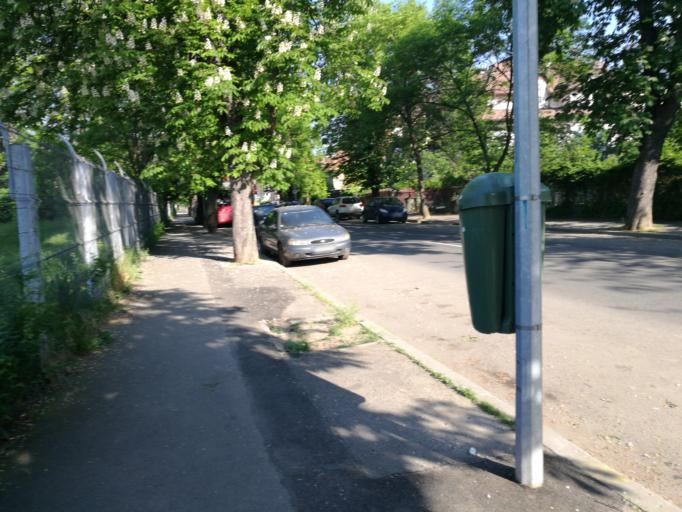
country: RO
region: Bucuresti
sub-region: Municipiul Bucuresti
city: Bucuresti
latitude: 44.4661
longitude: 26.0634
